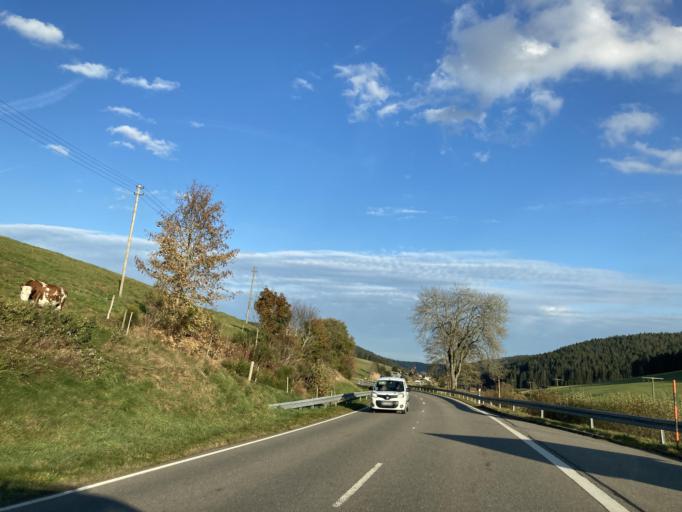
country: DE
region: Baden-Wuerttemberg
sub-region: Freiburg Region
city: Furtwangen im Schwarzwald
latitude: 48.0043
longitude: 8.2296
